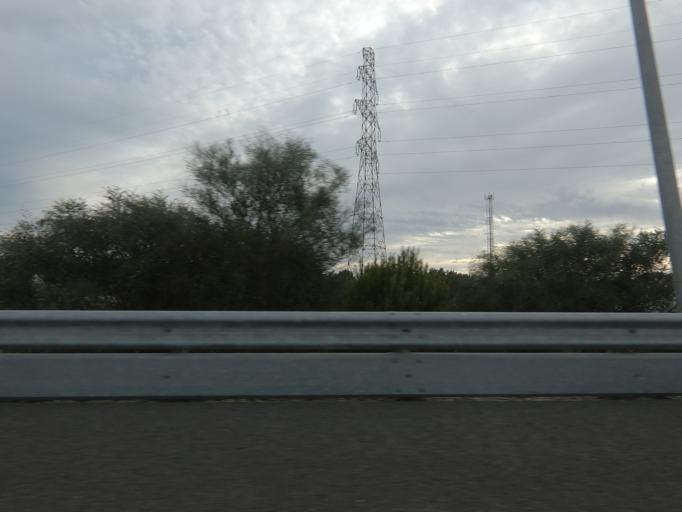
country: PT
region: Setubal
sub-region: Almada
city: Charneca
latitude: 38.6173
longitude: -9.1778
